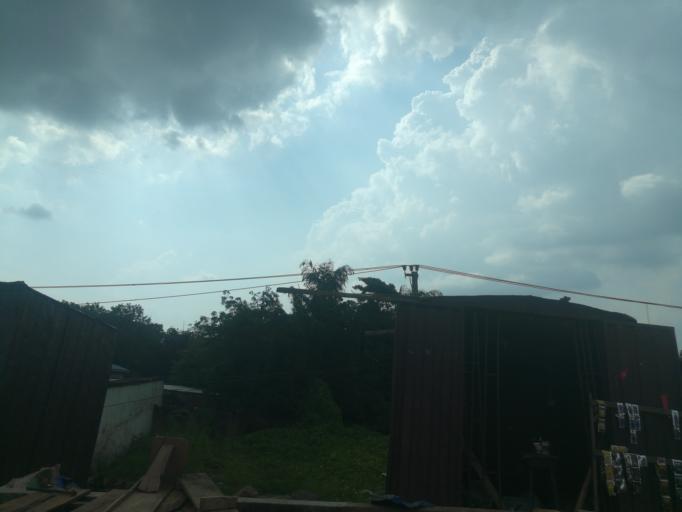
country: NG
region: Oyo
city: Ibadan
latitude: 7.3440
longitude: 3.8773
